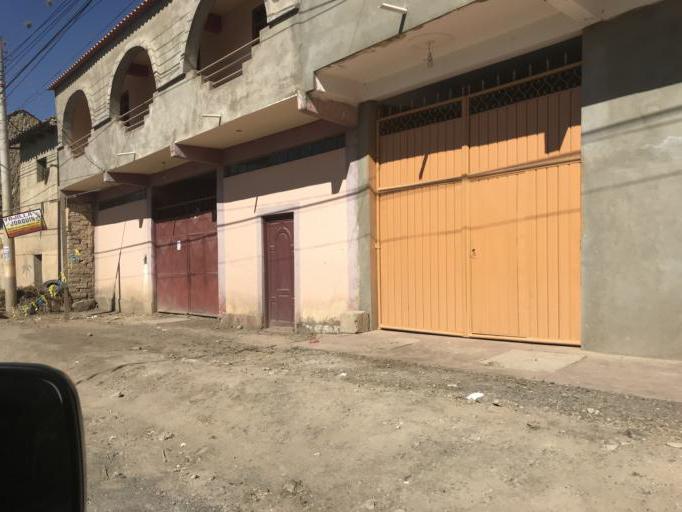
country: BO
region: Cochabamba
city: Punata
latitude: -17.5622
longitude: -65.8777
